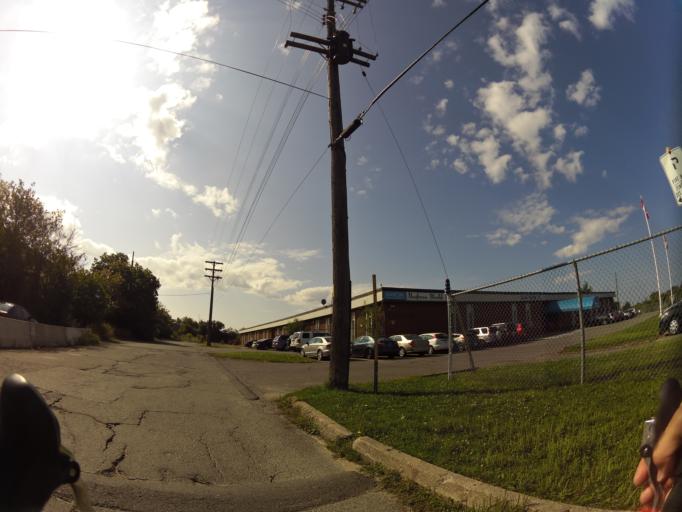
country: CA
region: Ontario
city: Ottawa
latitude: 45.3763
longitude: -75.6673
